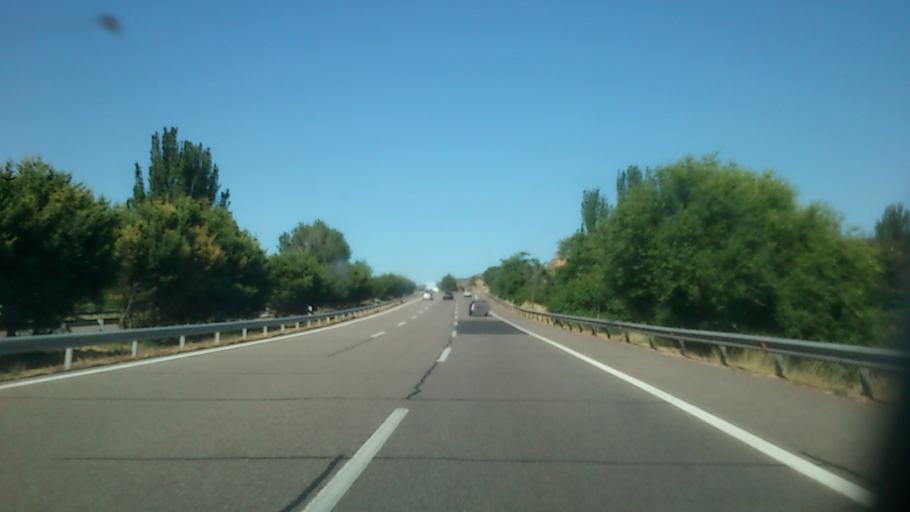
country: ES
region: Aragon
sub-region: Provincia de Zaragoza
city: Calatayud
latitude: 41.3597
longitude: -1.6022
